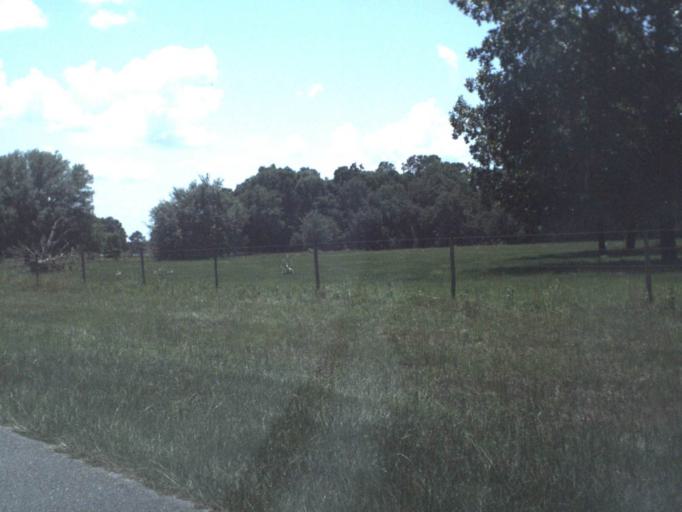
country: US
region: Florida
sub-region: Alachua County
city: High Springs
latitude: 29.9033
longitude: -82.7229
